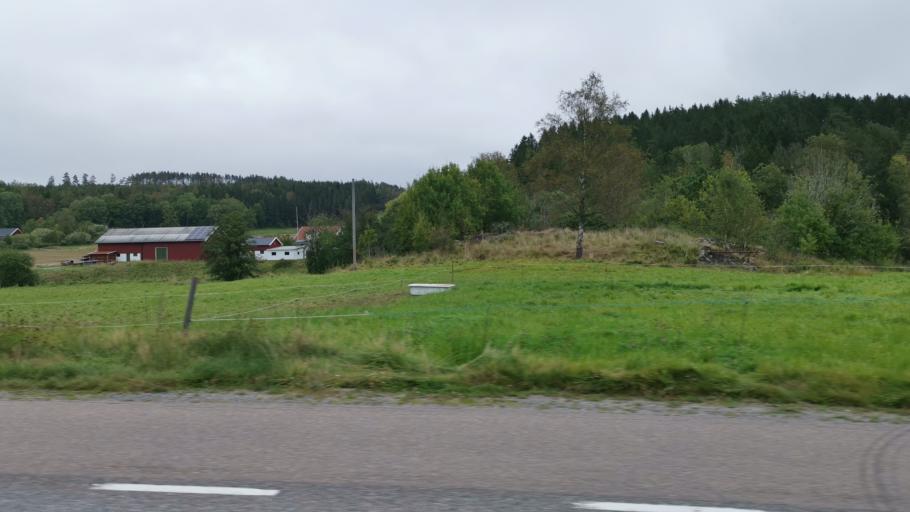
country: SE
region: Vaestra Goetaland
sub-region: Sotenas Kommun
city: Hunnebostrand
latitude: 58.5617
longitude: 11.3959
